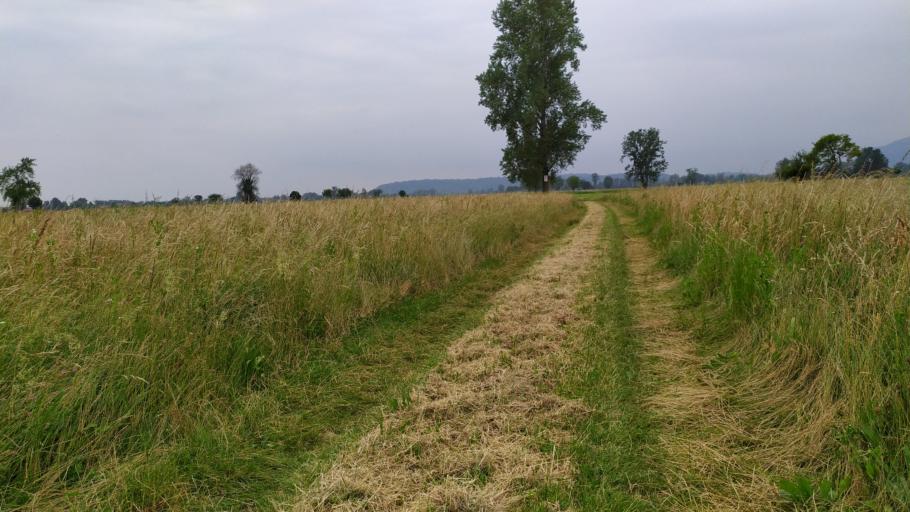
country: IT
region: Friuli Venezia Giulia
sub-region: Provincia di Udine
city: Osoppo
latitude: 46.2379
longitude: 13.0673
